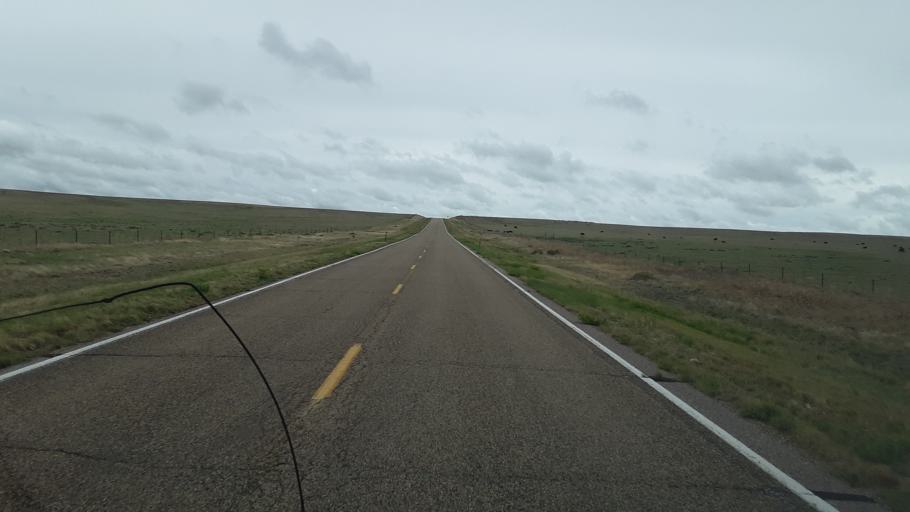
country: US
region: Colorado
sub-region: Lincoln County
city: Hugo
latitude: 38.8498
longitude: -103.3916
